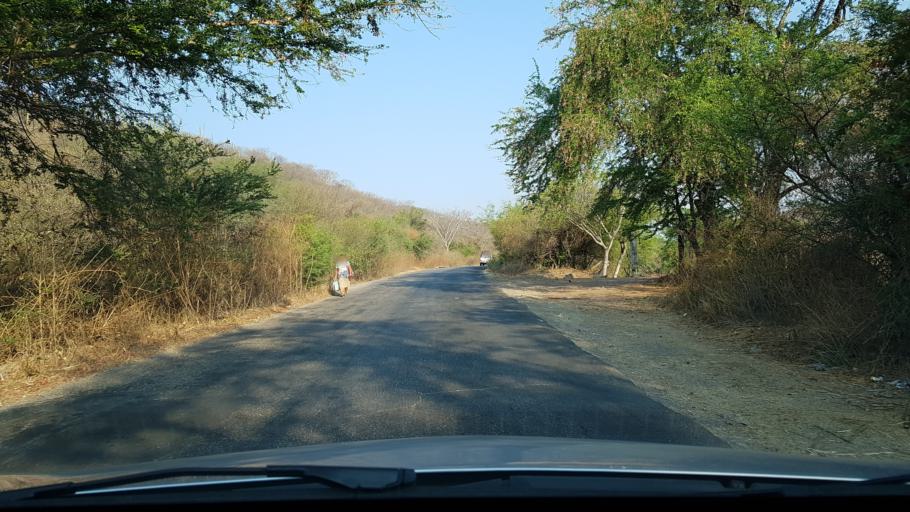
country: MX
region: Morelos
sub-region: Tepalcingo
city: Zacapalco
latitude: 18.6542
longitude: -99.0362
